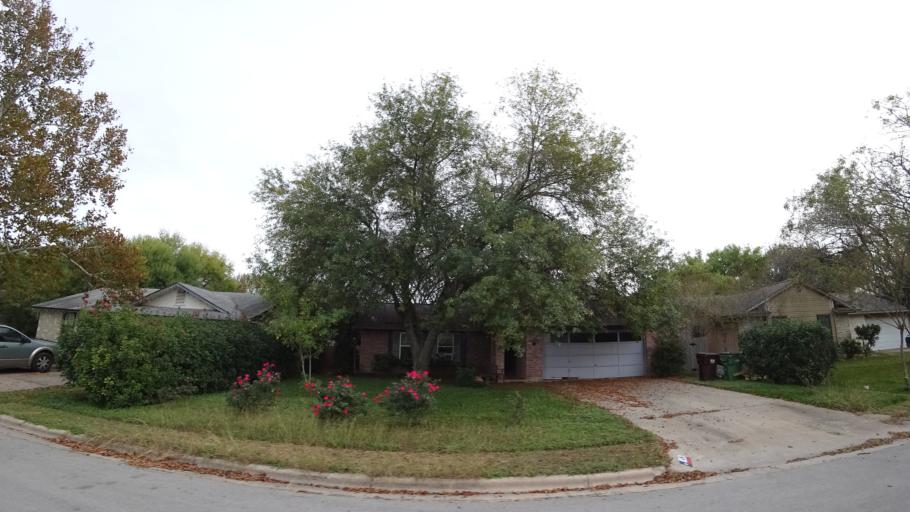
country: US
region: Texas
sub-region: Williamson County
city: Round Rock
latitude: 30.5066
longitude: -97.6641
